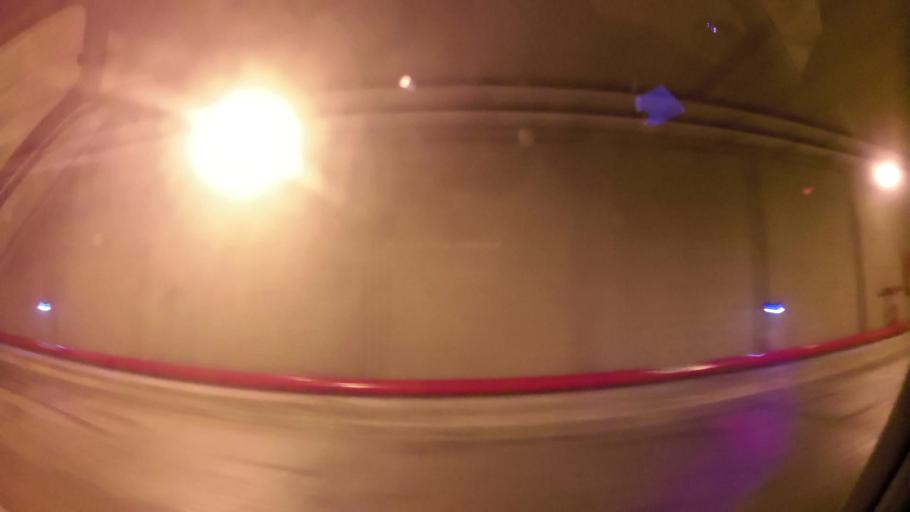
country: CO
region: Bolivar
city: Cartagena
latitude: 10.4462
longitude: -75.5224
